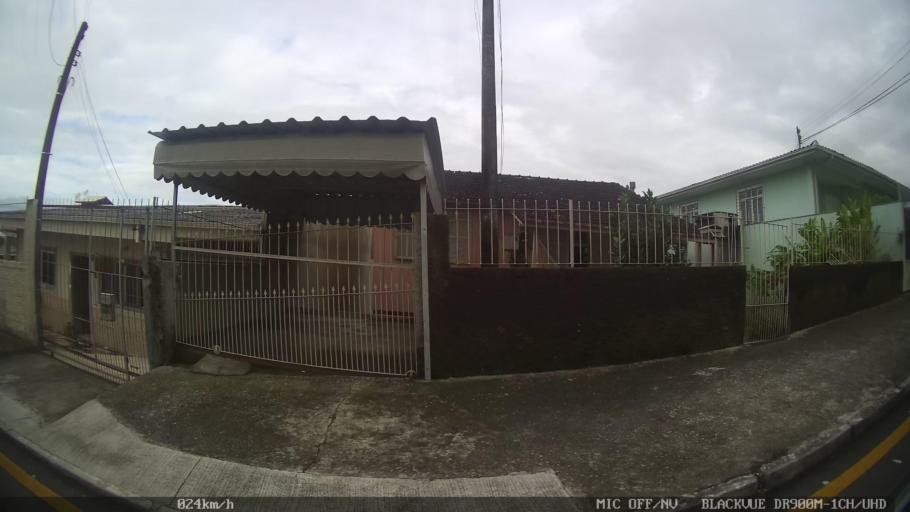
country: BR
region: Santa Catarina
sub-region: Sao Jose
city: Campinas
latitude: -27.5723
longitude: -48.6262
